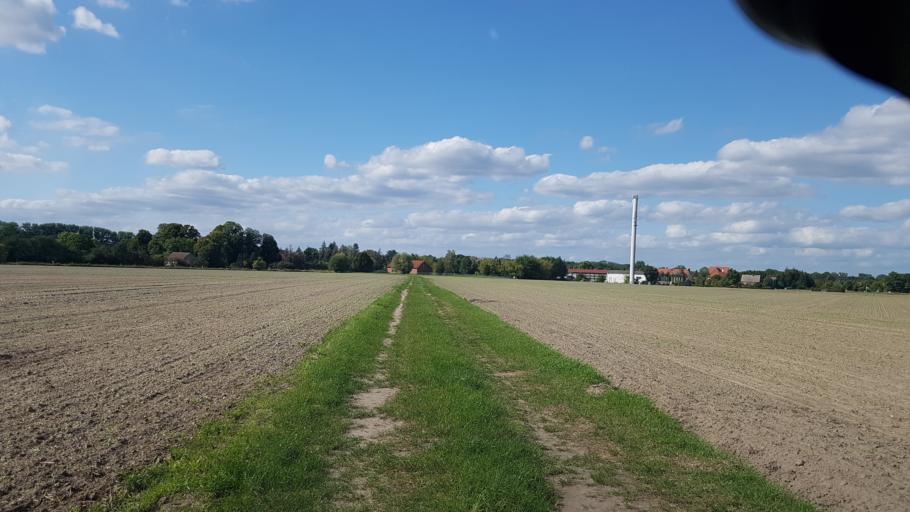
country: DE
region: Brandenburg
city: Sonnewalde
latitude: 51.6893
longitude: 13.6530
